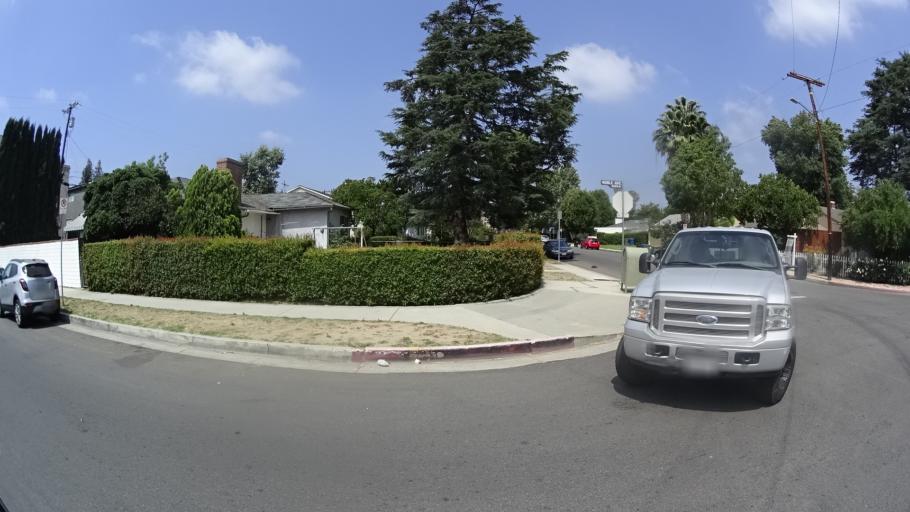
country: US
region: California
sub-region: Los Angeles County
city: Van Nuys
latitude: 34.1729
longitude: -118.4618
